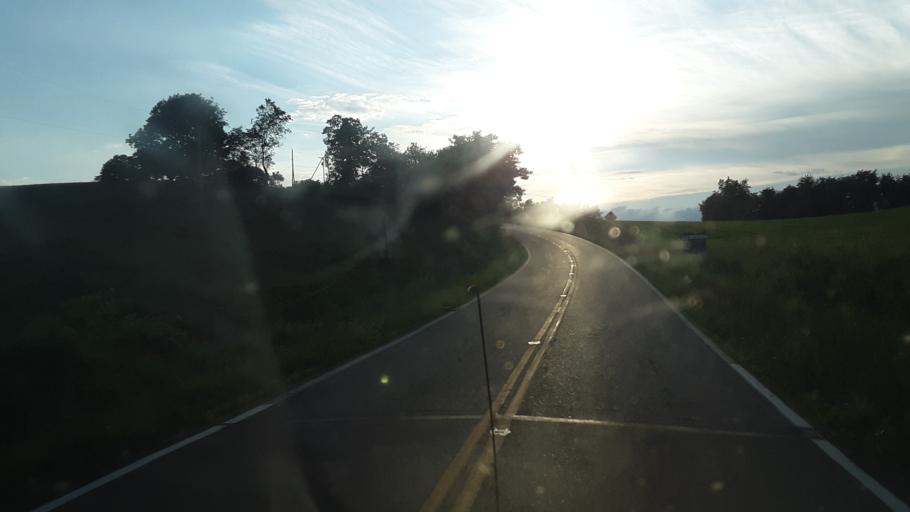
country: US
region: Ohio
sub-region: Harrison County
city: Cadiz
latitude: 40.4013
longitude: -81.0215
